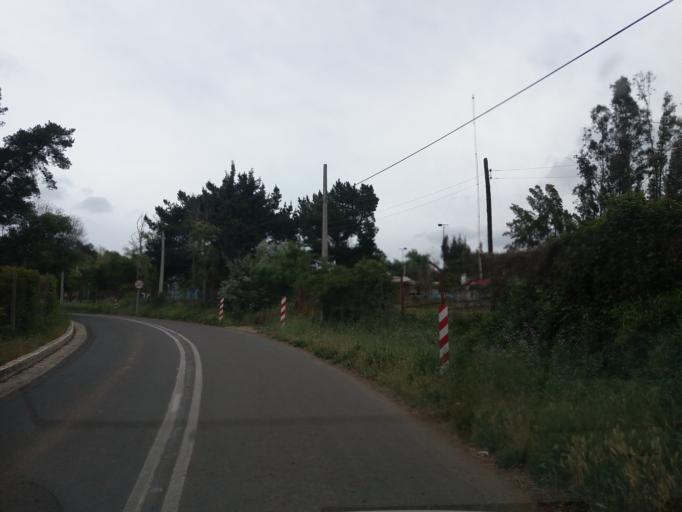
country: CL
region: Valparaiso
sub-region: Provincia de Quillota
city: Quillota
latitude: -32.8911
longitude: -71.3097
